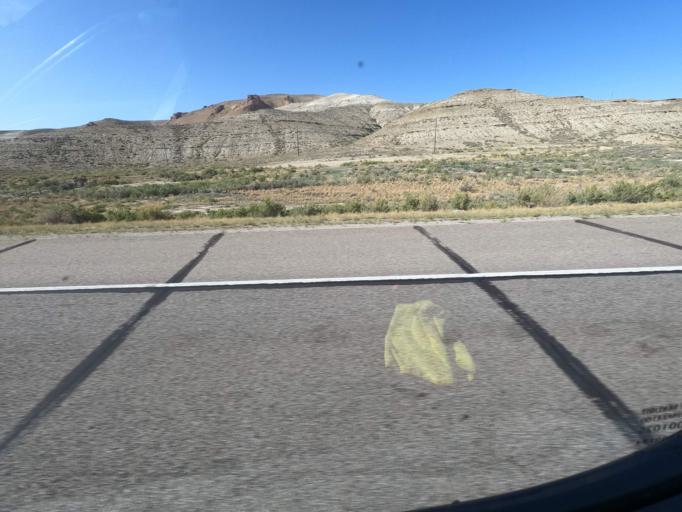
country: US
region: Wyoming
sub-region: Sweetwater County
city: Green River
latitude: 41.5332
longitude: -109.3871
